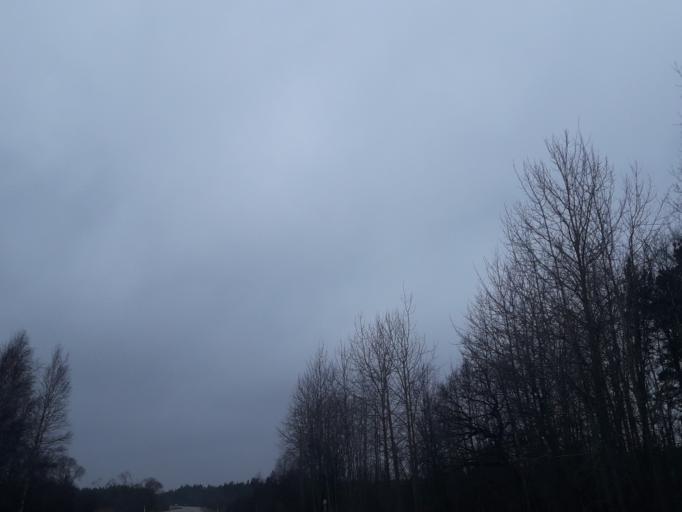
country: EE
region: Saare
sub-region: Kuressaare linn
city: Kuressaare
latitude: 58.2822
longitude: 22.4266
